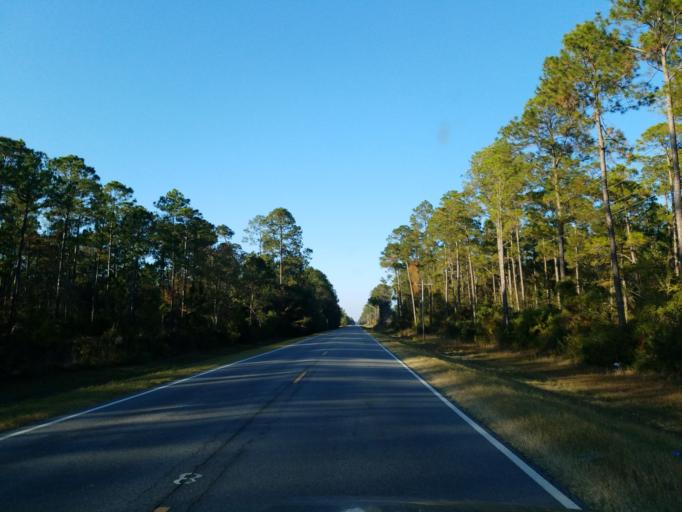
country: US
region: Georgia
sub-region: Lanier County
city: Lakeland
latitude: 31.0913
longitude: -83.0775
